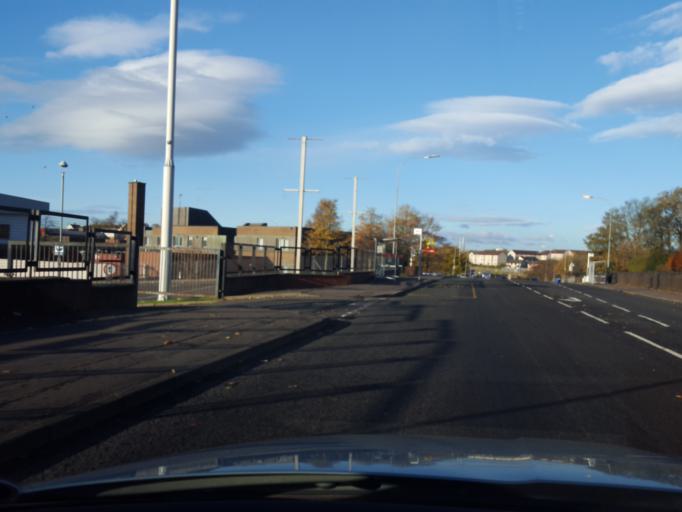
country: GB
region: Scotland
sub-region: North Lanarkshire
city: Chryston
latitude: 55.8689
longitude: -4.1176
